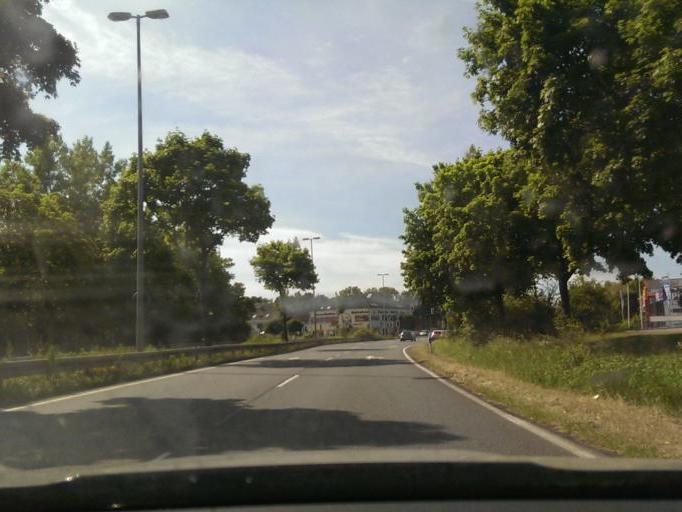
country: DE
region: Lower Saxony
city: Hildesheim
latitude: 52.1665
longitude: 9.9643
